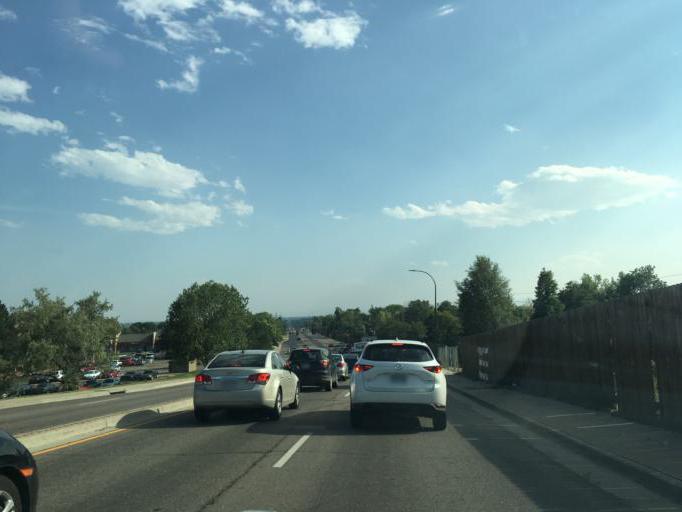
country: US
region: Colorado
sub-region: Adams County
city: Westminster
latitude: 39.8511
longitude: -105.0530
